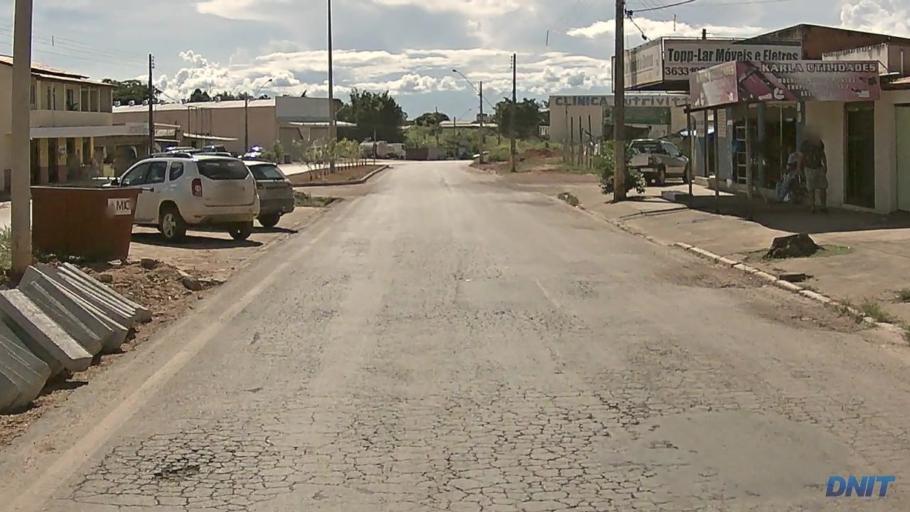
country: BR
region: Goias
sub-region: Padre Bernardo
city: Padre Bernardo
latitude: -15.1668
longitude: -48.2900
